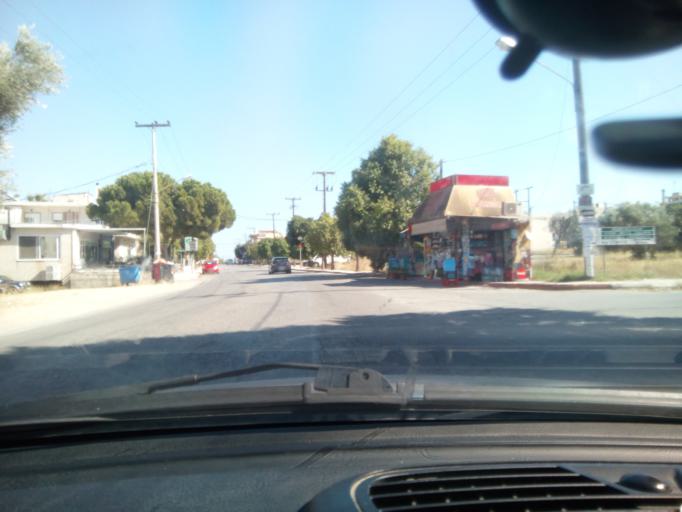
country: GR
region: Central Greece
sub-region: Nomos Evvoias
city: Vasilikon
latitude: 38.4234
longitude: 23.6754
